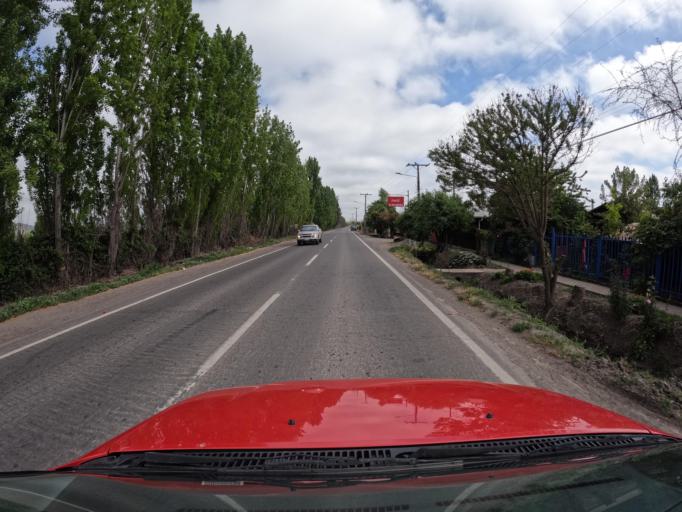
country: CL
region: O'Higgins
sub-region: Provincia de Colchagua
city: Santa Cruz
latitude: -34.6875
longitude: -71.3274
